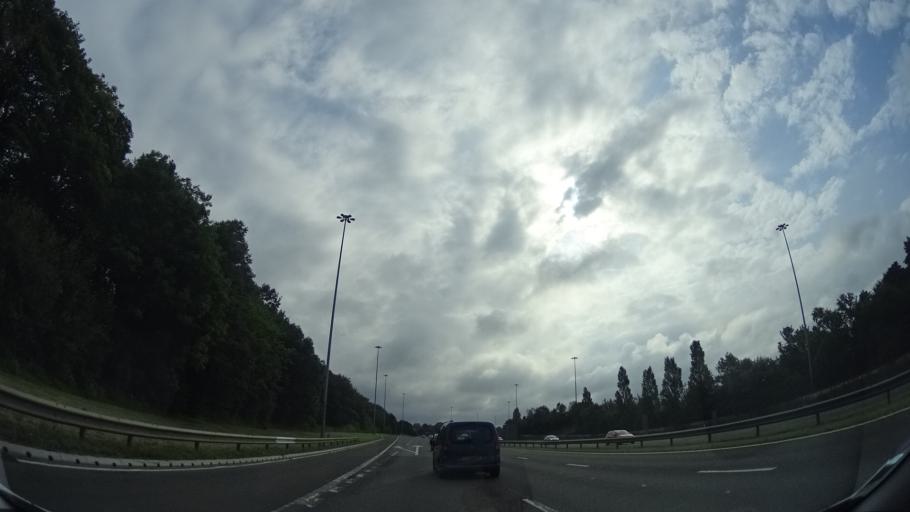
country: GB
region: England
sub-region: Knowsley
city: Huyton
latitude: 53.4080
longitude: -2.8786
